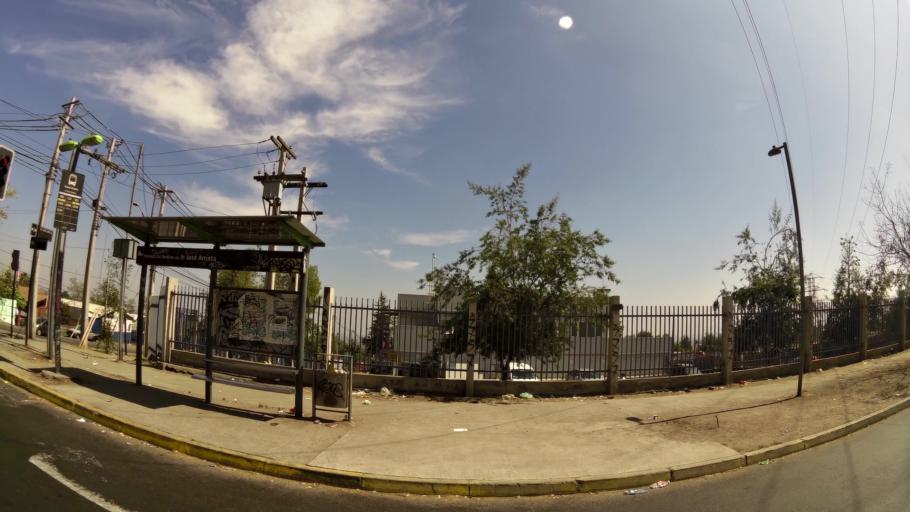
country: CL
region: Santiago Metropolitan
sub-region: Provincia de Santiago
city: Villa Presidente Frei, Nunoa, Santiago, Chile
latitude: -33.4653
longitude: -70.5313
